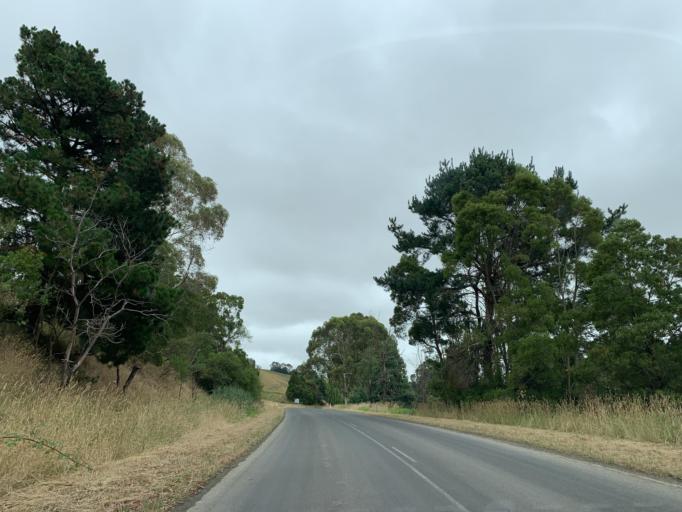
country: AU
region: Victoria
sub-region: Baw Baw
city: Warragul
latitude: -38.3205
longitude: 145.8309
